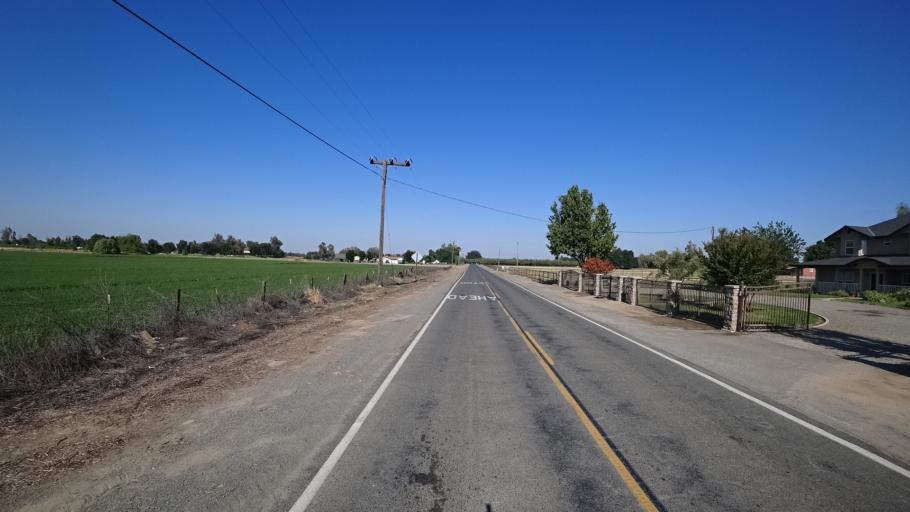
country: US
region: California
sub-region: Kings County
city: Lemoore
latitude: 36.3658
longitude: -119.8120
